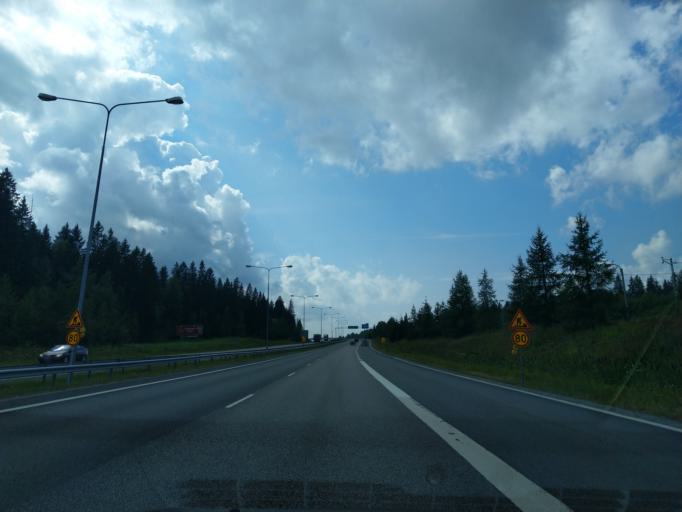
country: FI
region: South Karelia
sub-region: Imatra
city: Imatra
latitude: 61.2000
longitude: 28.8060
